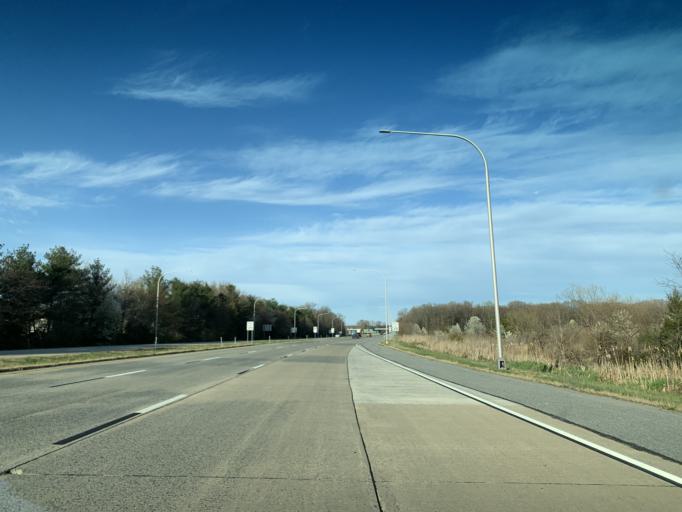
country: US
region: Delaware
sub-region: Kent County
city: Cheswold
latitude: 39.2012
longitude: -75.5540
